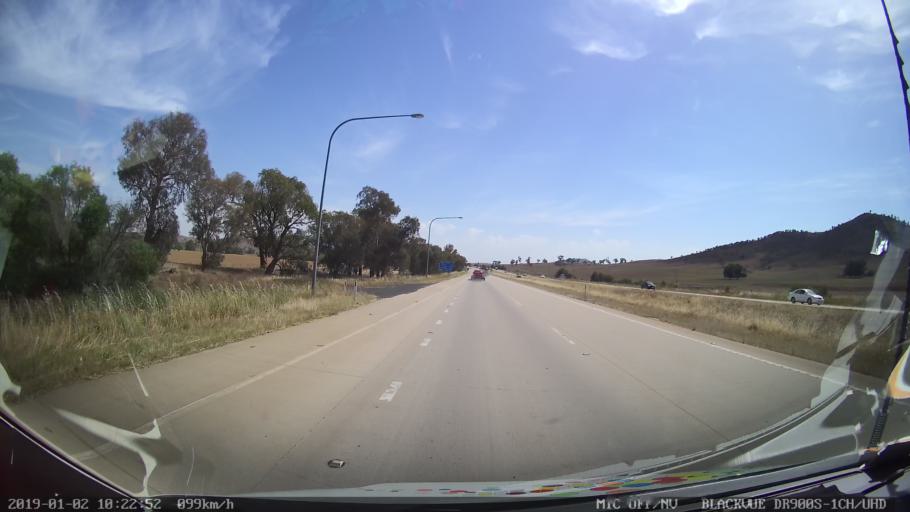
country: AU
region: New South Wales
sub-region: Gundagai
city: Gundagai
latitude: -34.9669
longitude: 148.1526
